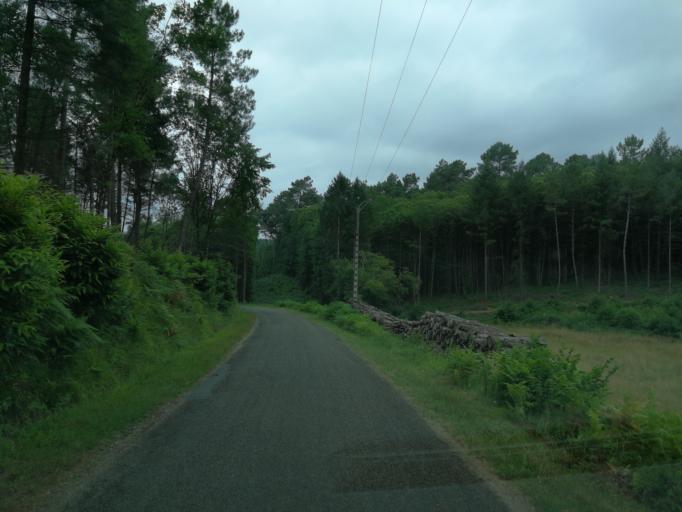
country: FR
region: Aquitaine
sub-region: Departement du Lot-et-Garonne
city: Montayral
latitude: 44.5603
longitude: 1.0745
